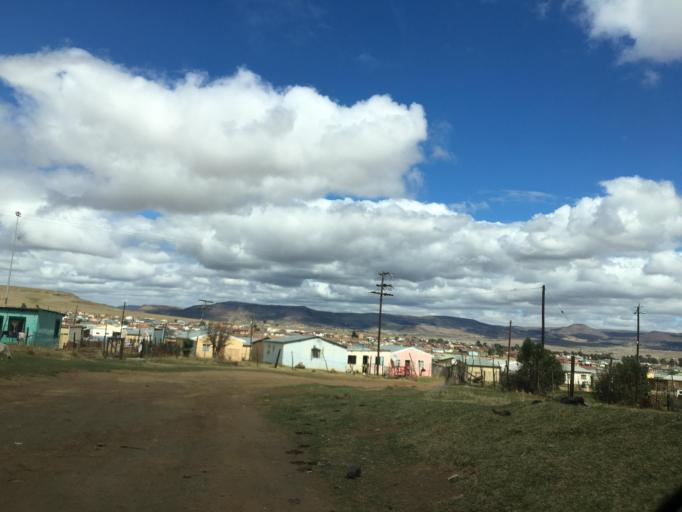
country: ZA
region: Eastern Cape
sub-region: Chris Hani District Municipality
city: Cala
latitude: -31.5310
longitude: 27.7021
